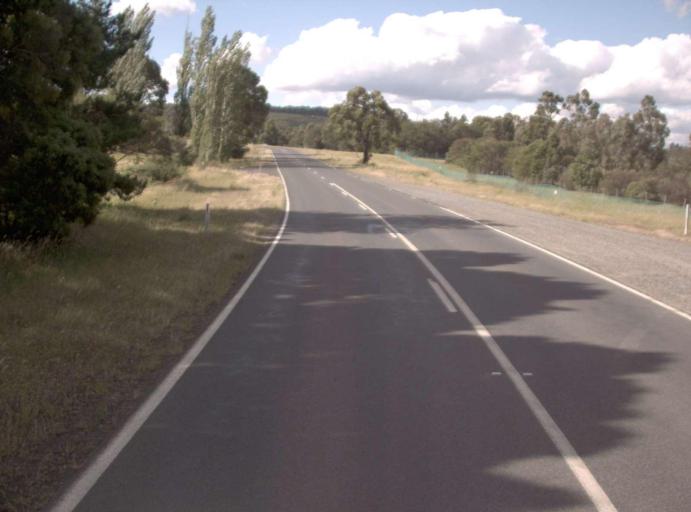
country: AU
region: Victoria
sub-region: Latrobe
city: Moe
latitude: -38.2005
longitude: 146.3280
